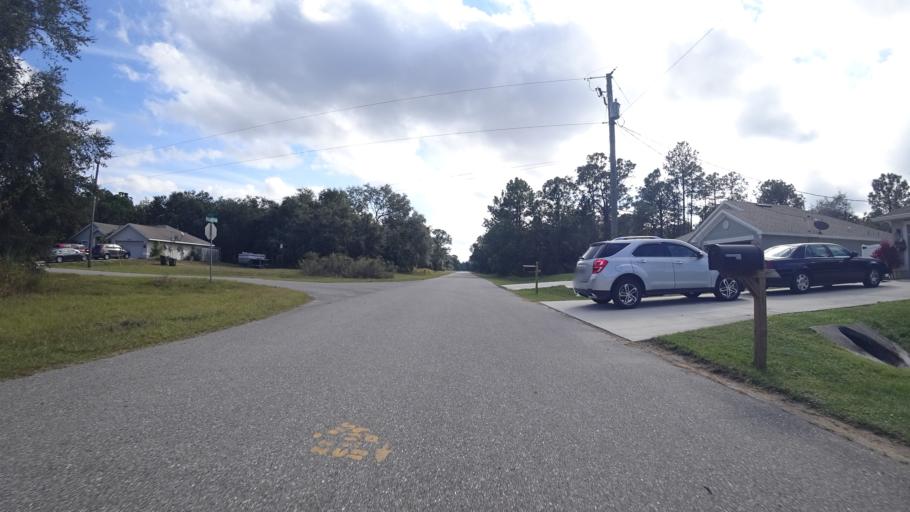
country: US
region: Florida
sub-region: Charlotte County
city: Port Charlotte
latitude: 27.0510
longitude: -82.1249
